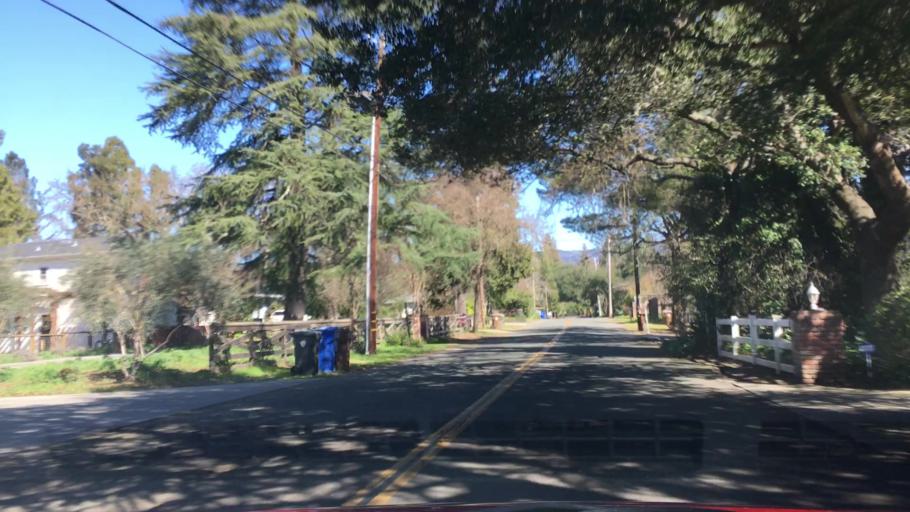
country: US
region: California
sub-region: Napa County
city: Napa
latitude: 38.3413
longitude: -122.2692
